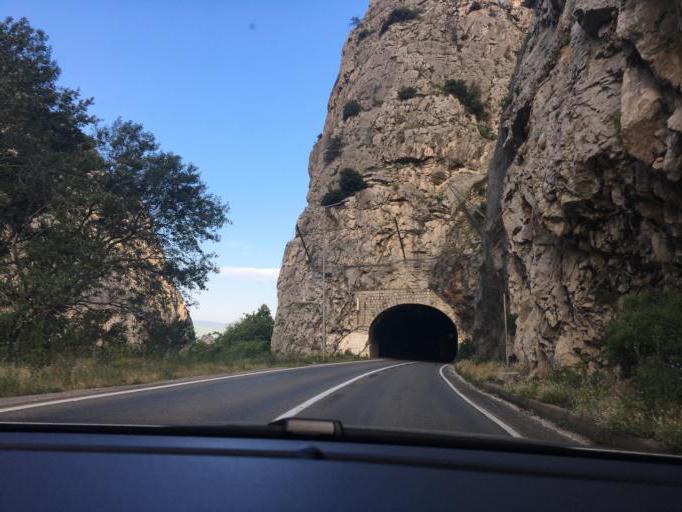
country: MK
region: Demir Kapija
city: Demir Kapija
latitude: 41.4058
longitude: 22.2647
